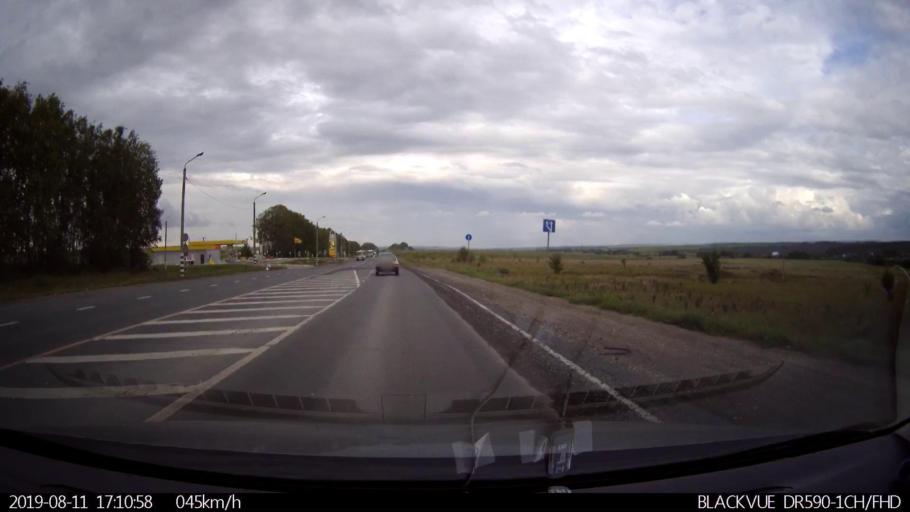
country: RU
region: Ulyanovsk
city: Mayna
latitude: 54.2997
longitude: 47.8799
